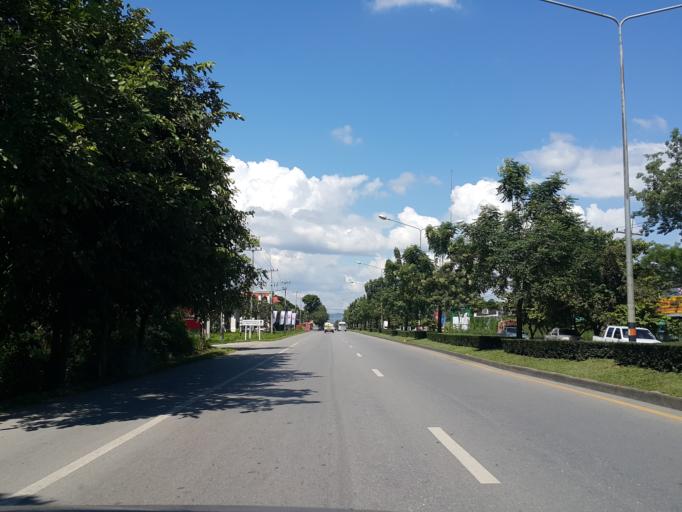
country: TH
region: Chiang Mai
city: San Sai
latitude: 18.8385
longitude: 99.0130
